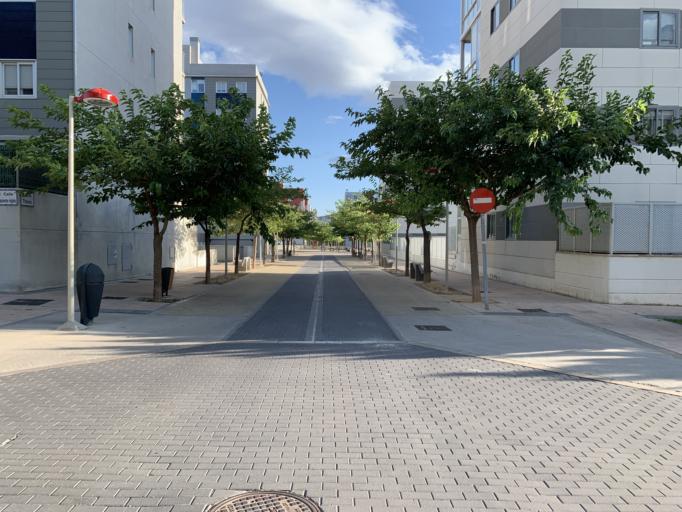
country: ES
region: Aragon
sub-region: Provincia de Zaragoza
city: Montecanal
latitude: 41.6247
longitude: -0.9313
